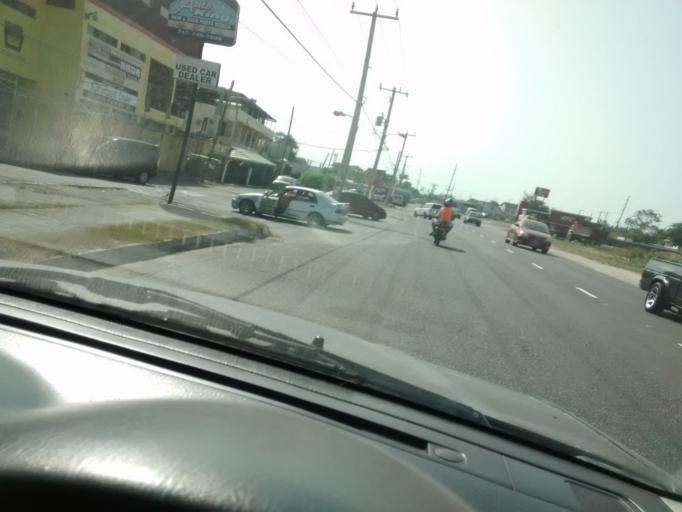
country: JM
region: Saint Catherine
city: Portmore
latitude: 17.9839
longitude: -76.8834
